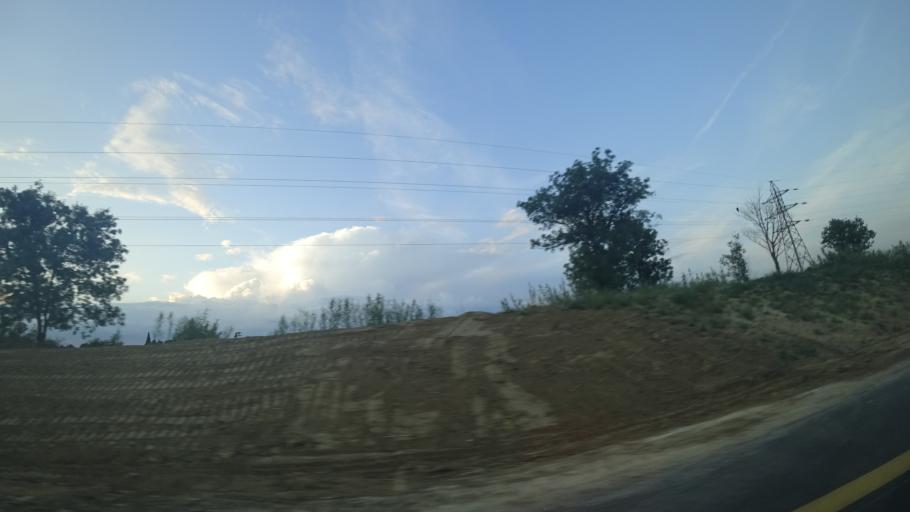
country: FR
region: Languedoc-Roussillon
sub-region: Departement de l'Herault
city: Boujan-sur-Libron
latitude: 43.3621
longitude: 3.2483
